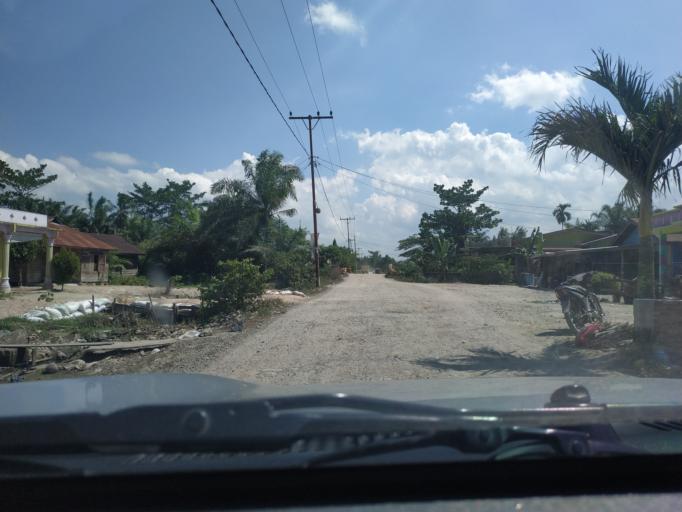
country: ID
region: North Sumatra
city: Tanjungbalai
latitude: 2.8810
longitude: 99.8615
